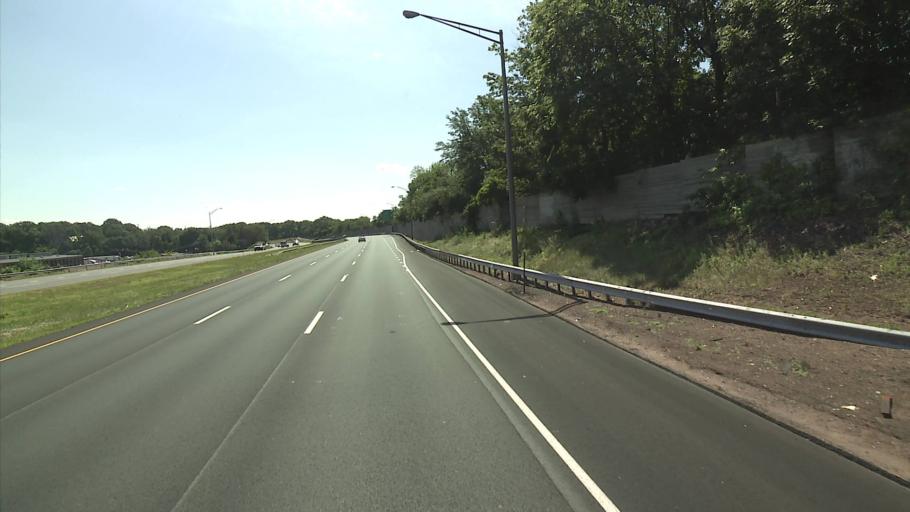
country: US
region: Connecticut
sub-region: Hartford County
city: New Britain
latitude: 41.6643
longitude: -72.8122
